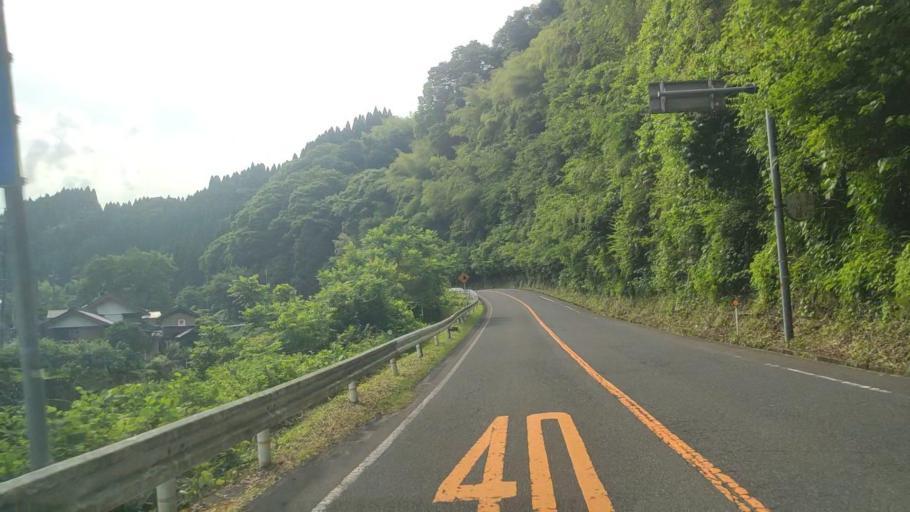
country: JP
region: Tottori
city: Tottori
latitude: 35.3330
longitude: 134.1298
